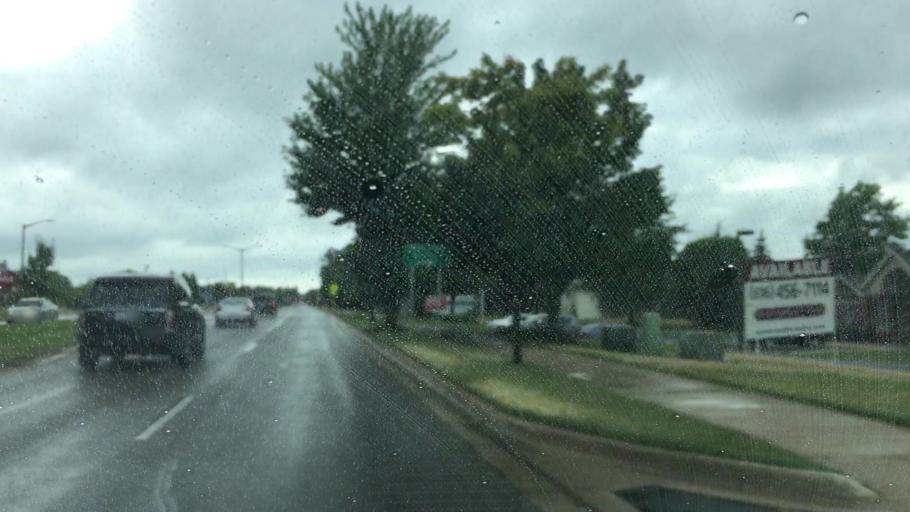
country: US
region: Michigan
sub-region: Ottawa County
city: Holland
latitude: 42.7833
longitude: -86.0709
